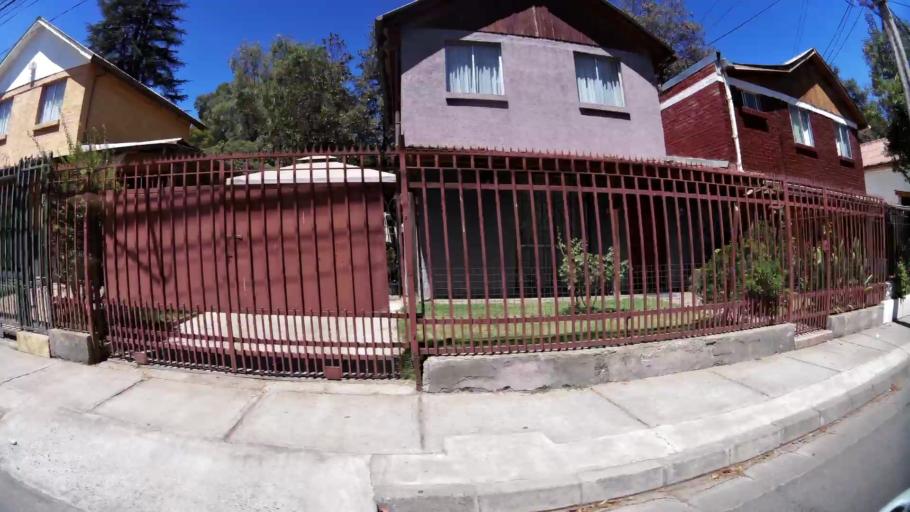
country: CL
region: O'Higgins
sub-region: Provincia de Cachapoal
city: Rancagua
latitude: -34.1586
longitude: -70.7507
